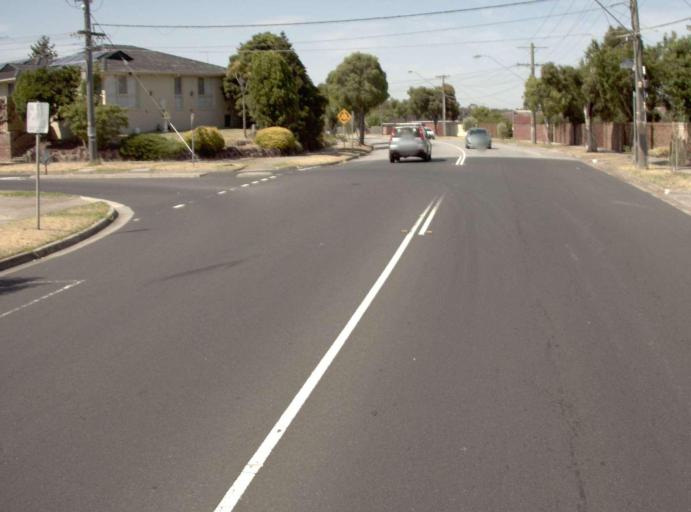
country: AU
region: Victoria
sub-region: Greater Dandenong
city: Noble Park North
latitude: -37.9542
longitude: 145.1909
